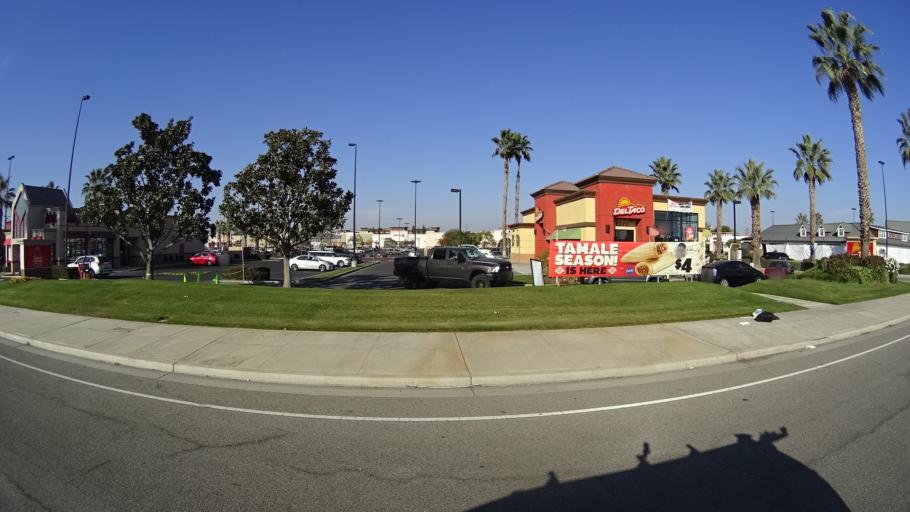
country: US
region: California
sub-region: Kern County
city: Greenacres
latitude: 35.3834
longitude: -119.0940
